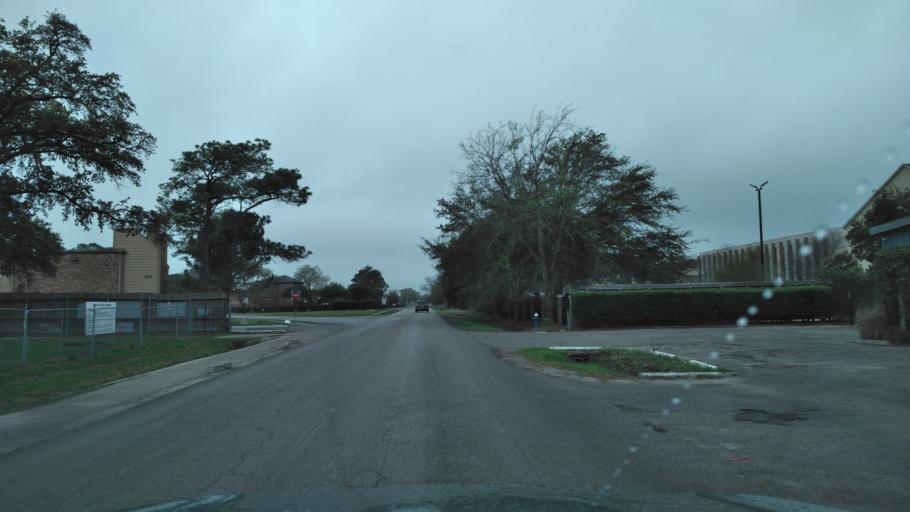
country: US
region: Texas
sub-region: Harris County
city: Piney Point Village
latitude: 29.7307
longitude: -95.4905
